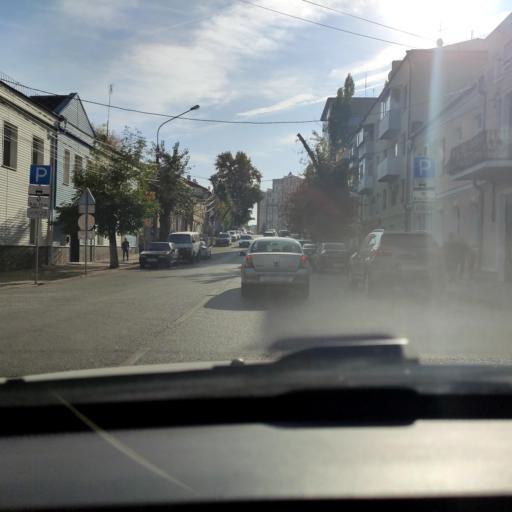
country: RU
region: Voronezj
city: Voronezh
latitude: 51.6753
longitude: 39.2168
